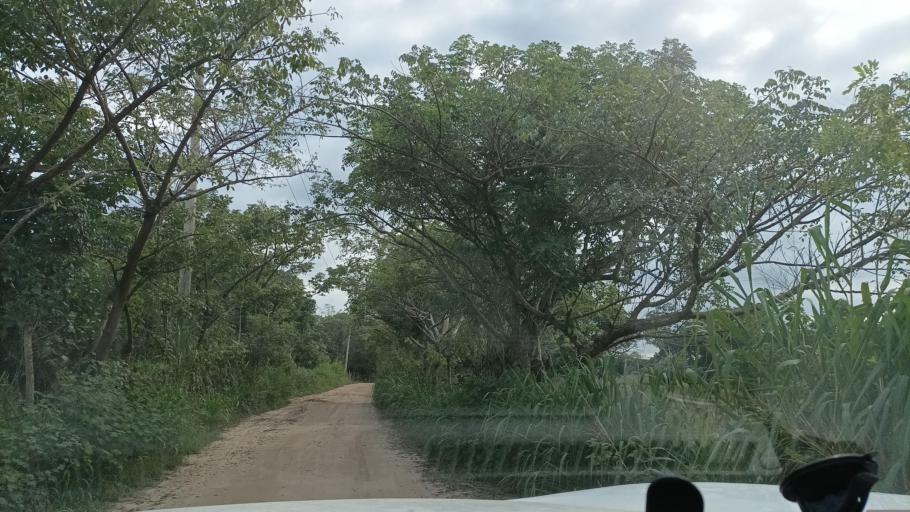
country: MX
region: Veracruz
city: Oluta
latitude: 17.9354
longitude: -94.8824
